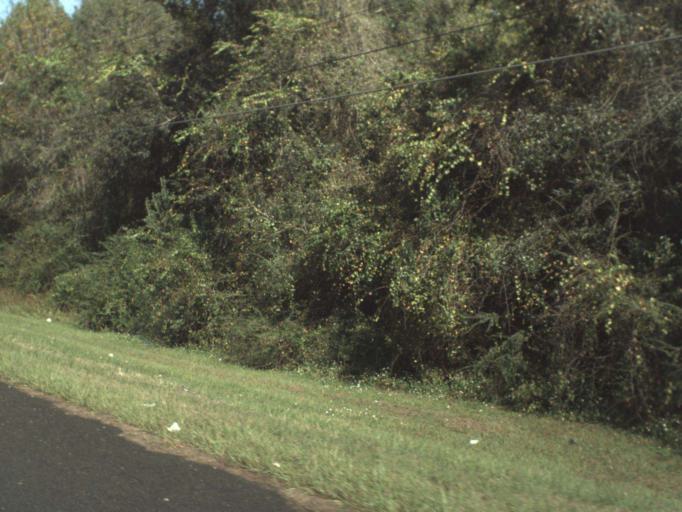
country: US
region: Florida
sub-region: Gadsden County
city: Quincy
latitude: 30.5722
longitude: -84.5506
